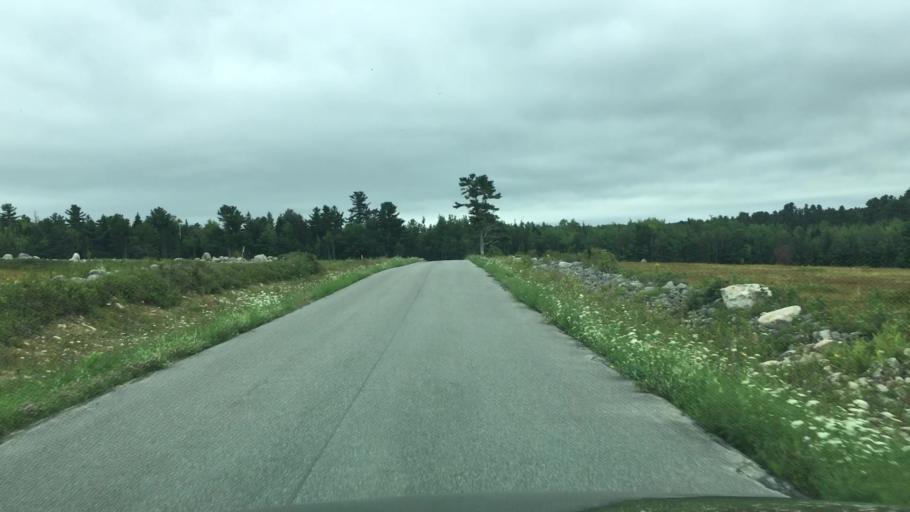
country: US
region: Maine
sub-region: Waldo County
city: Stockton Springs
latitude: 44.5240
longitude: -68.8816
